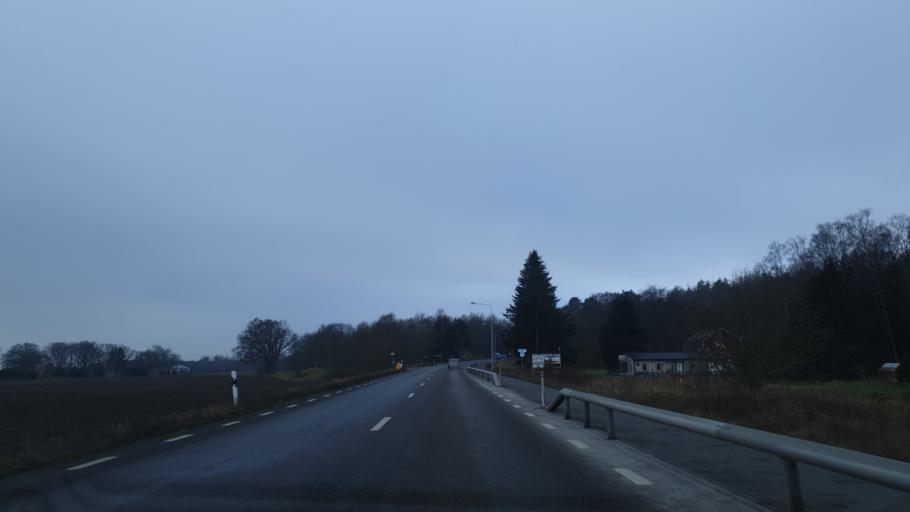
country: SE
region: Blekinge
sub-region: Solvesborgs Kommun
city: Soelvesborg
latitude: 56.0961
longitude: 14.6598
